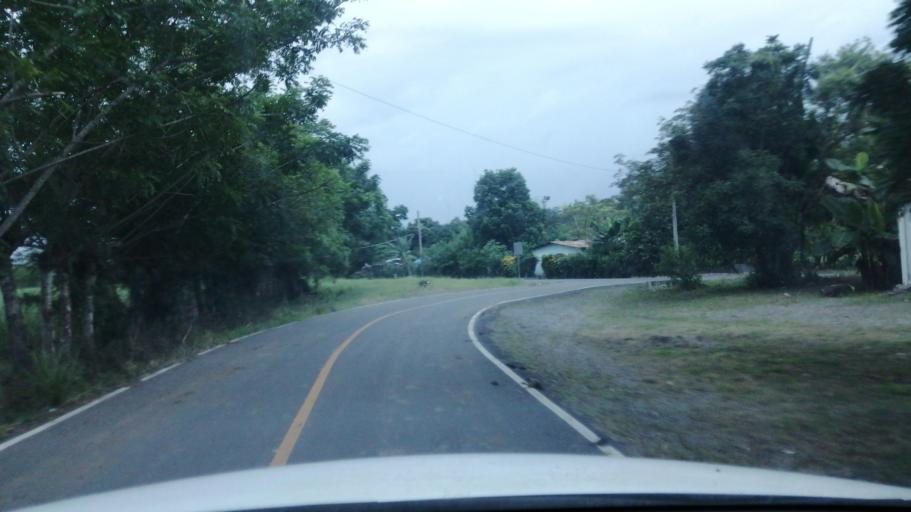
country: PA
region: Chiriqui
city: Alanje
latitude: 8.4197
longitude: -82.5042
